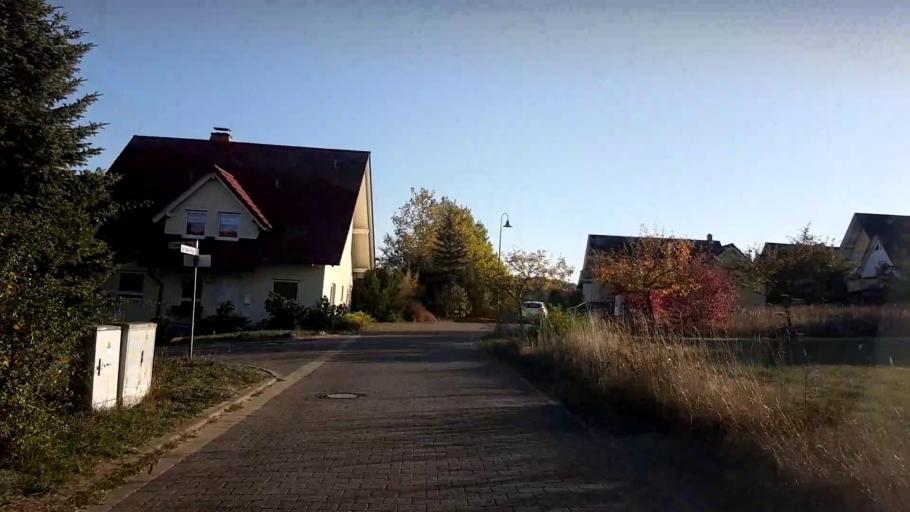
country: DE
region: Bavaria
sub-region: Upper Franconia
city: Walsdorf
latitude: 49.8736
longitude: 10.7898
